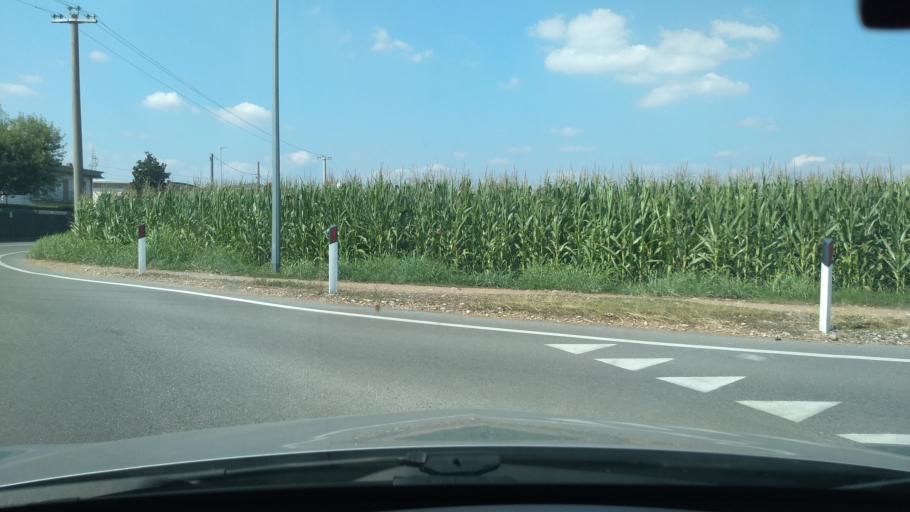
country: IT
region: Lombardy
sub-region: Provincia di Bergamo
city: Zanica
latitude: 45.6401
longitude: 9.6760
